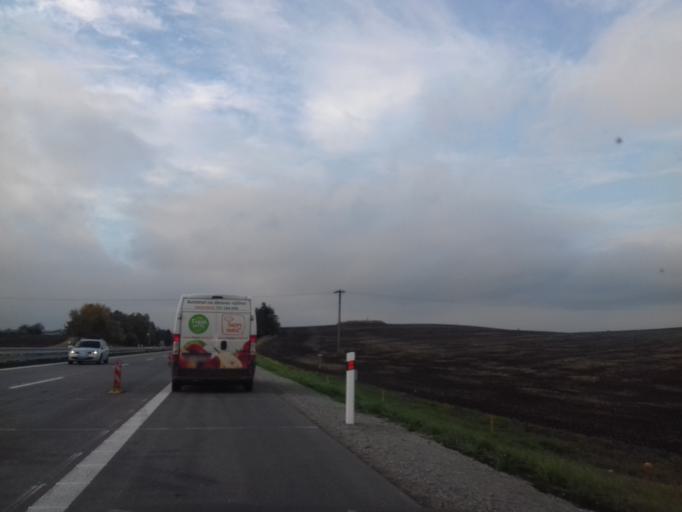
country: CZ
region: South Moravian
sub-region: Okres Brno-Venkov
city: Blucina
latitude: 49.0541
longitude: 16.6720
